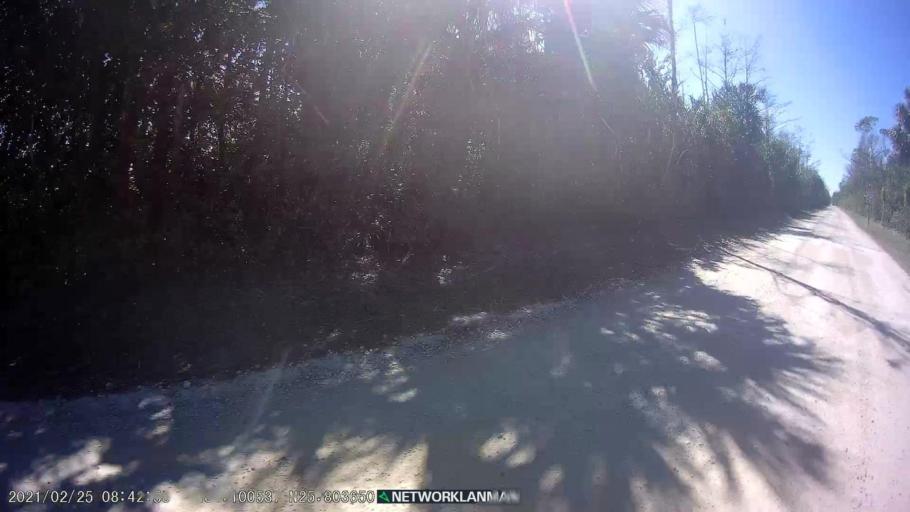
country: US
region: Florida
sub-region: Collier County
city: Marco
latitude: 25.8036
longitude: -81.1005
